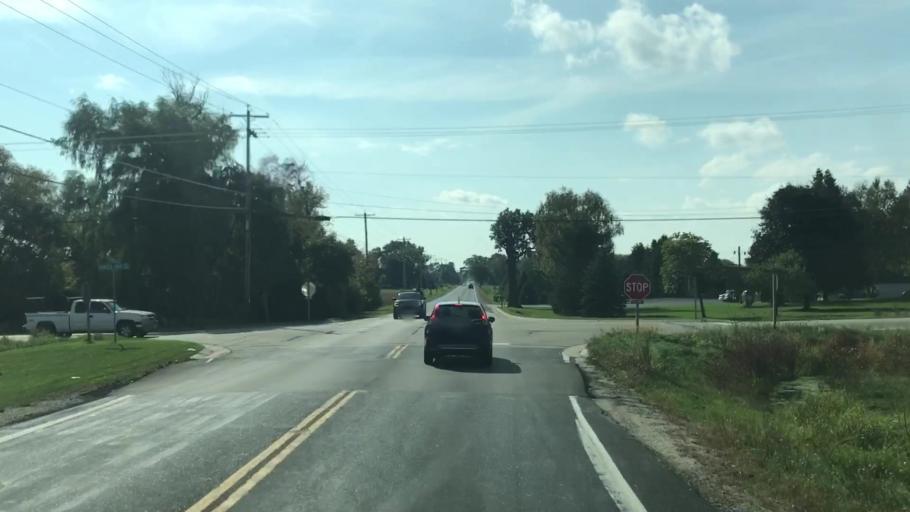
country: US
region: Wisconsin
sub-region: Ozaukee County
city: Mequon
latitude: 43.2072
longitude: -88.0435
